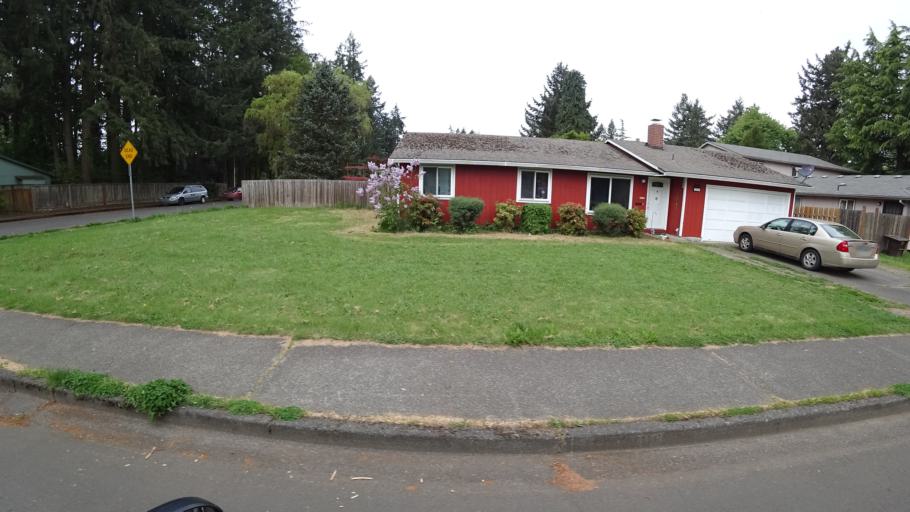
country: US
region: Oregon
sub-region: Washington County
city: Hillsboro
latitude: 45.5418
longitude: -122.9984
